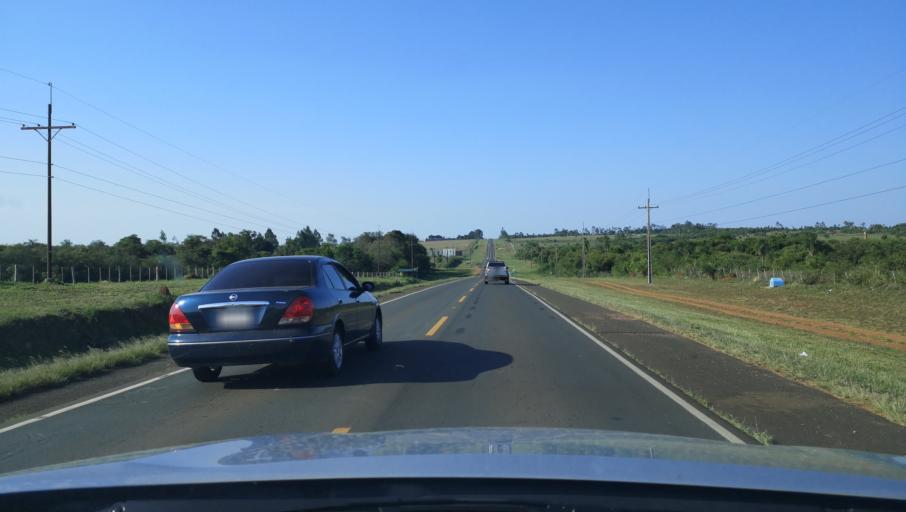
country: PY
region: Misiones
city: Santa Maria
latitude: -26.8357
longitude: -57.0336
